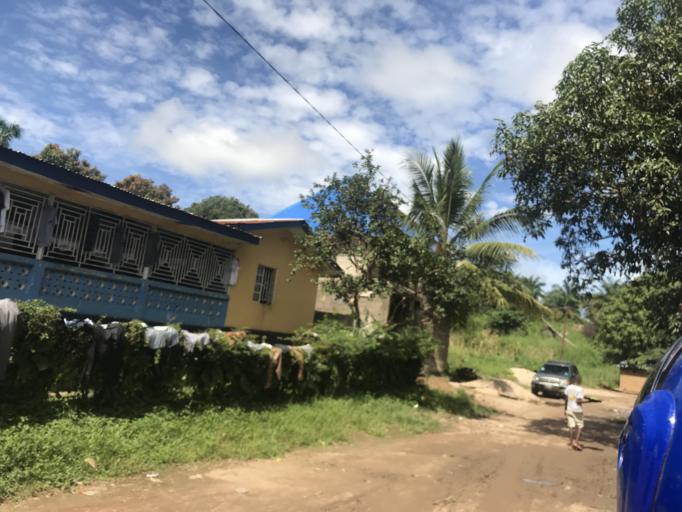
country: SL
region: Eastern Province
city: Koidu
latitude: 8.6475
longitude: -10.9878
